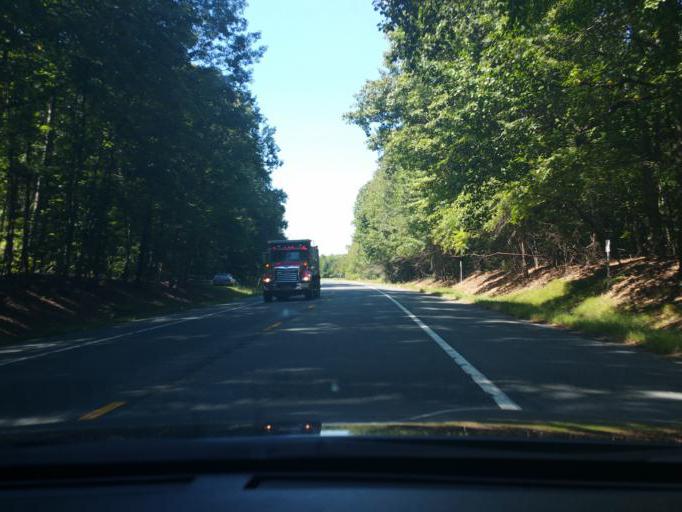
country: US
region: Maryland
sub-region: Harford County
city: Aberdeen
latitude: 39.5783
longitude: -76.1928
